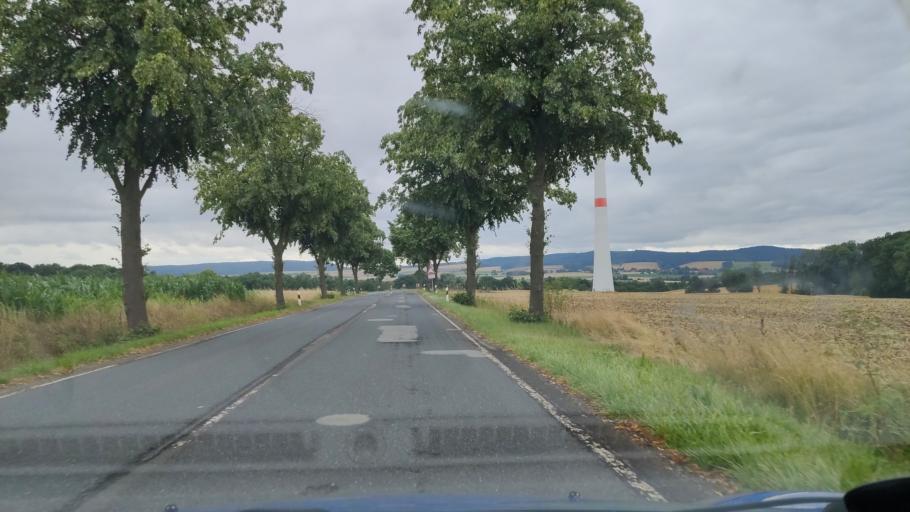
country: DE
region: Lower Saxony
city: Coppenbrugge
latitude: 52.1208
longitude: 9.5045
